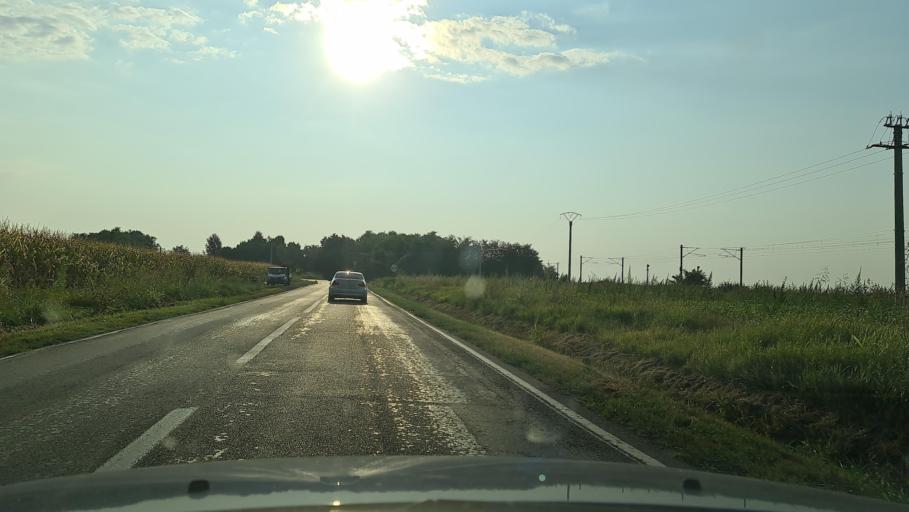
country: RO
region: Calarasi
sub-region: Oras Lehliu Gara
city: Razvani
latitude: 44.4368
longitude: 26.8868
